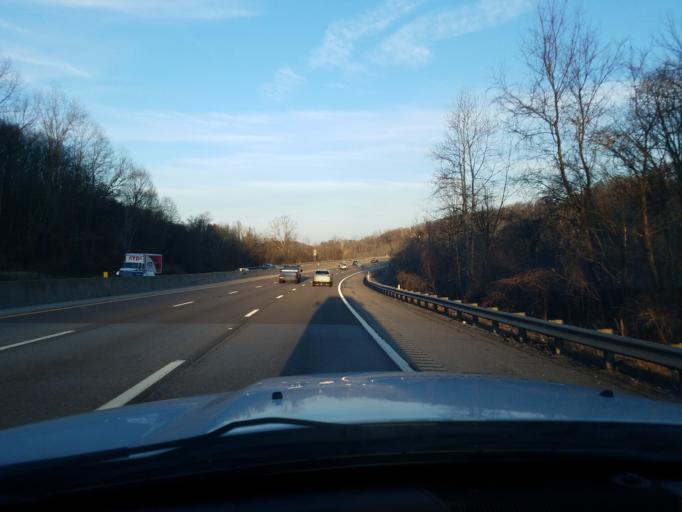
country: US
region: West Virginia
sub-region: Kanawha County
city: Nitro
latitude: 38.4282
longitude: -81.8212
